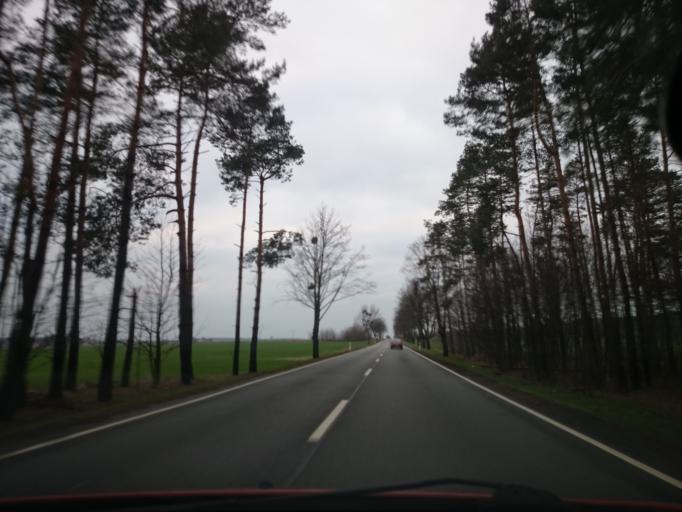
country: PL
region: Opole Voivodeship
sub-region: Powiat opolski
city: Niemodlin
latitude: 50.6094
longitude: 17.5570
